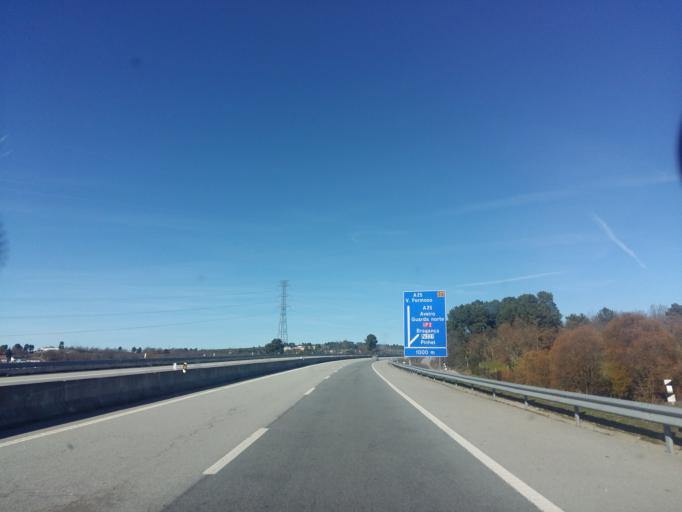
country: PT
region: Guarda
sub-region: Guarda
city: Sequeira
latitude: 40.5490
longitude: -7.2166
